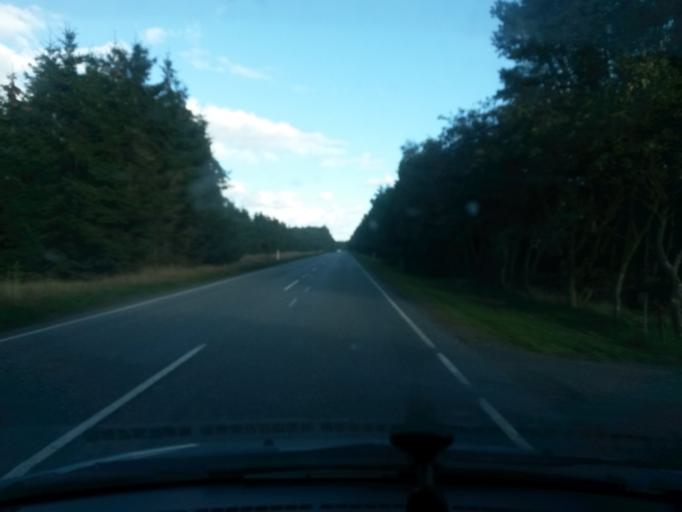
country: DK
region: Central Jutland
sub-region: Viborg Kommune
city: Karup
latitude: 56.3084
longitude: 9.1914
